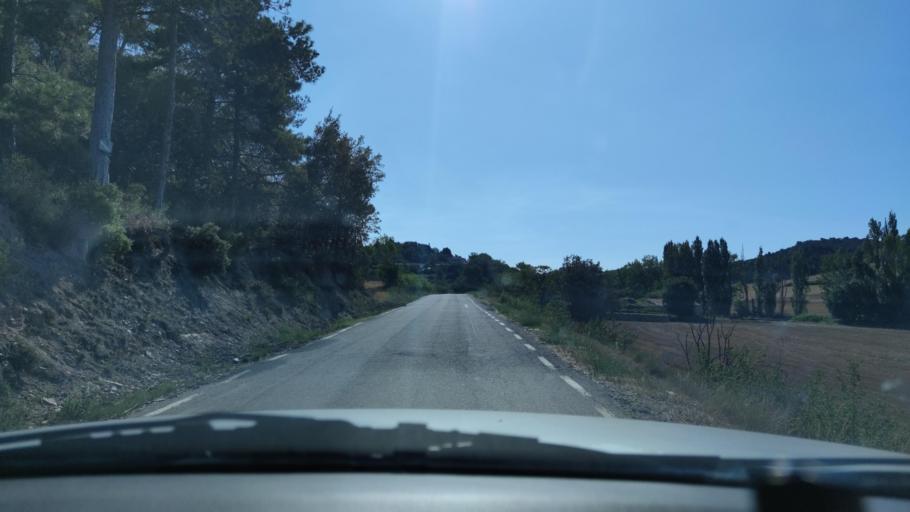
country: ES
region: Catalonia
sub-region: Provincia de Barcelona
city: Pujalt
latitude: 41.6885
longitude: 1.3838
